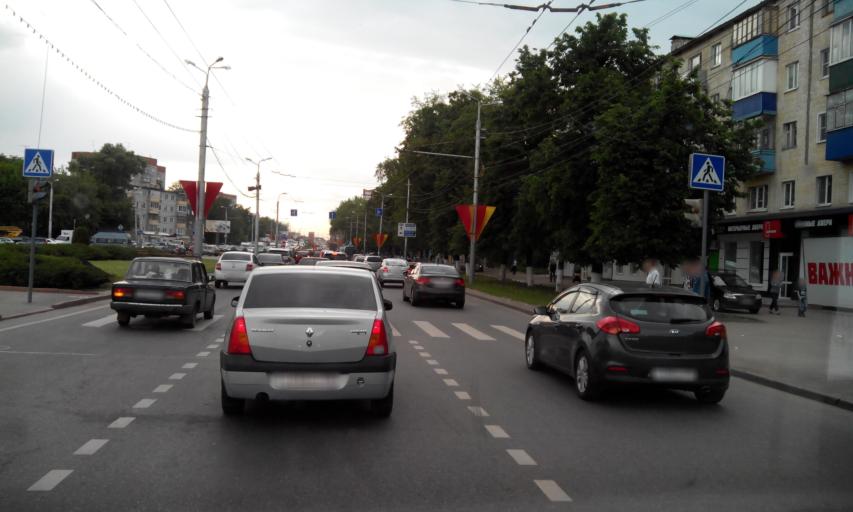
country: RU
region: Penza
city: Penza
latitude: 53.2140
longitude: 44.9890
